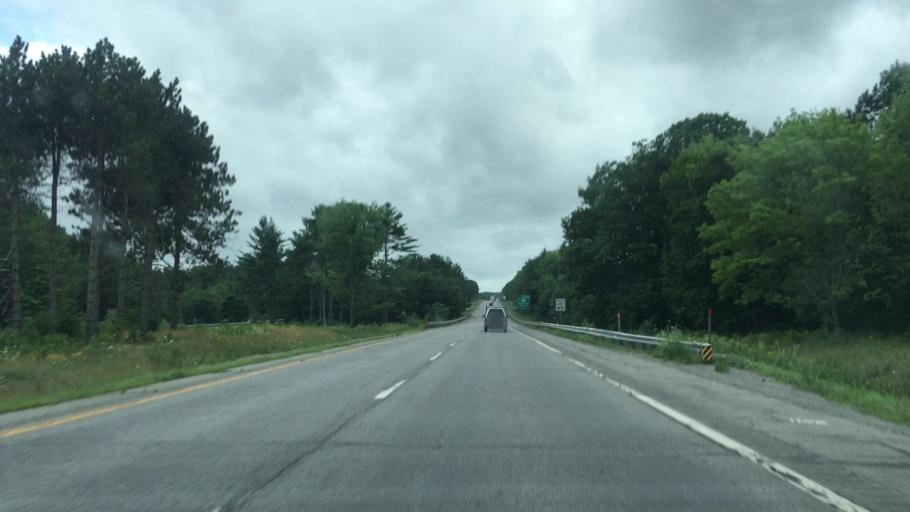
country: US
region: Maine
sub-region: Somerset County
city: Fairfield
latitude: 44.5868
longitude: -69.6224
